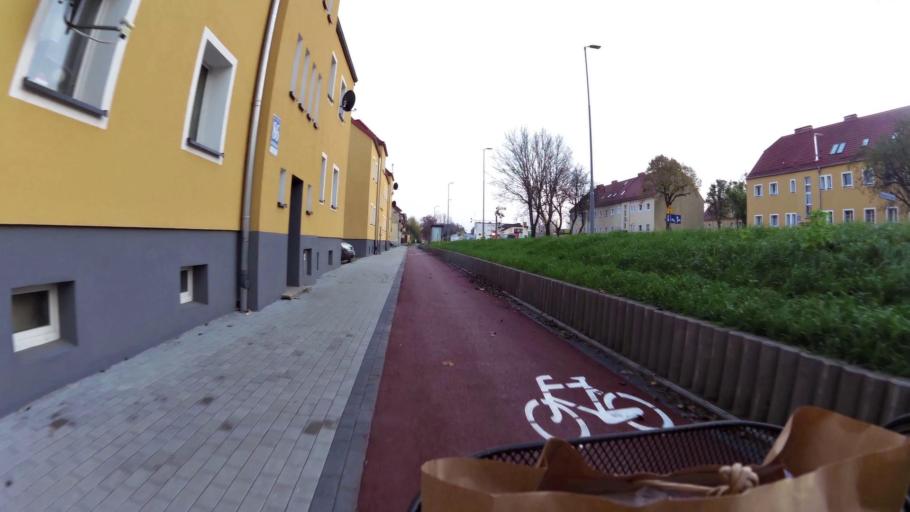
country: PL
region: West Pomeranian Voivodeship
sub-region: Koszalin
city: Koszalin
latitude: 54.2042
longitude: 16.1585
